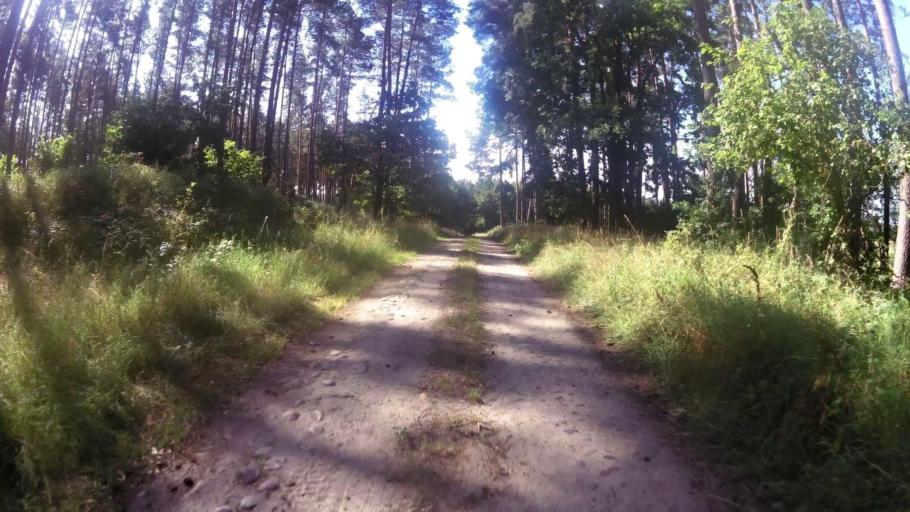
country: PL
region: West Pomeranian Voivodeship
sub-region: Powiat drawski
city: Drawsko Pomorskie
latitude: 53.5252
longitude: 15.7070
